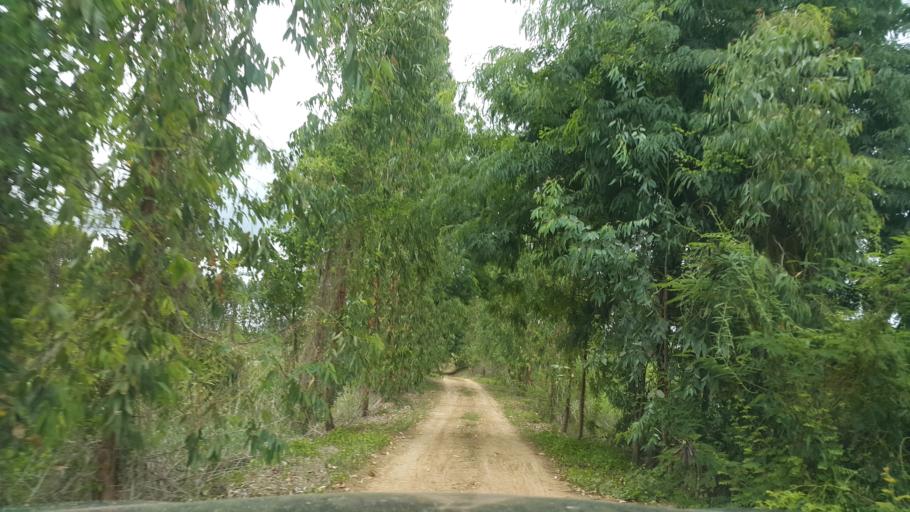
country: TH
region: Sukhothai
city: Sukhothai
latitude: 17.0279
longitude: 99.7985
